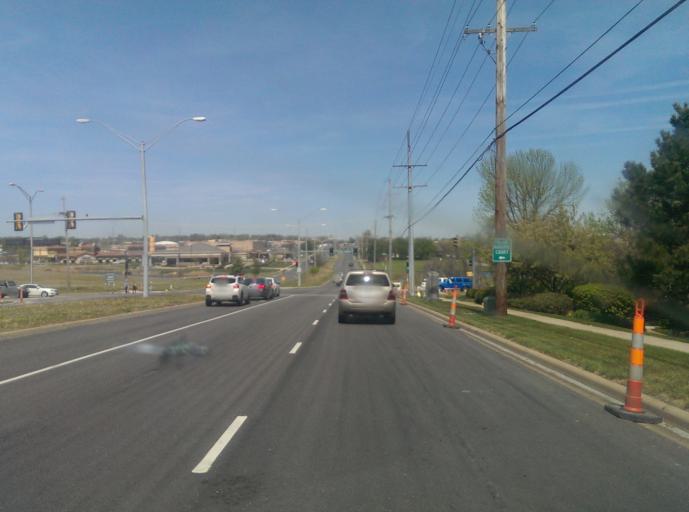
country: US
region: Kansas
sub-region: Johnson County
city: Overland Park
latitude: 38.9049
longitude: -94.6677
